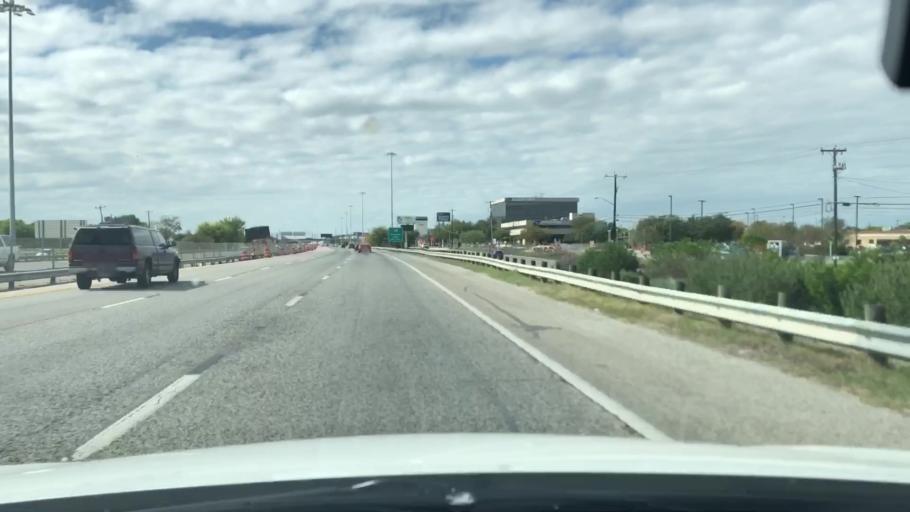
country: US
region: Texas
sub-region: Bexar County
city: Lackland Air Force Base
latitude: 29.4023
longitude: -98.6300
